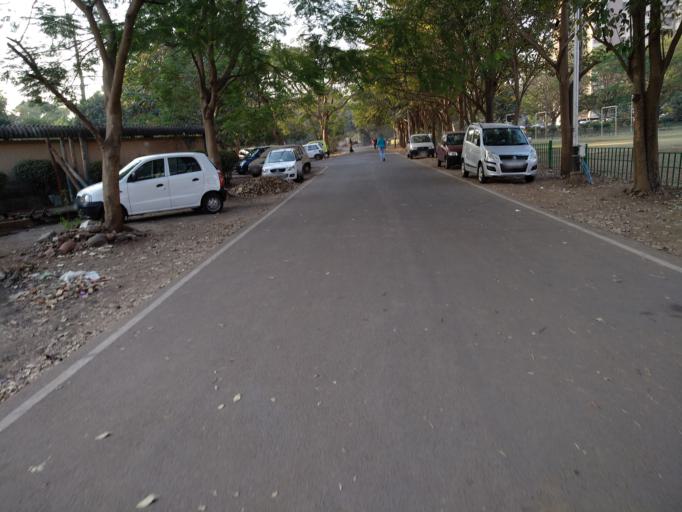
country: IN
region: Maharashtra
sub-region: Mumbai Suburban
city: Mumbai
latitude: 19.0366
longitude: 72.9266
